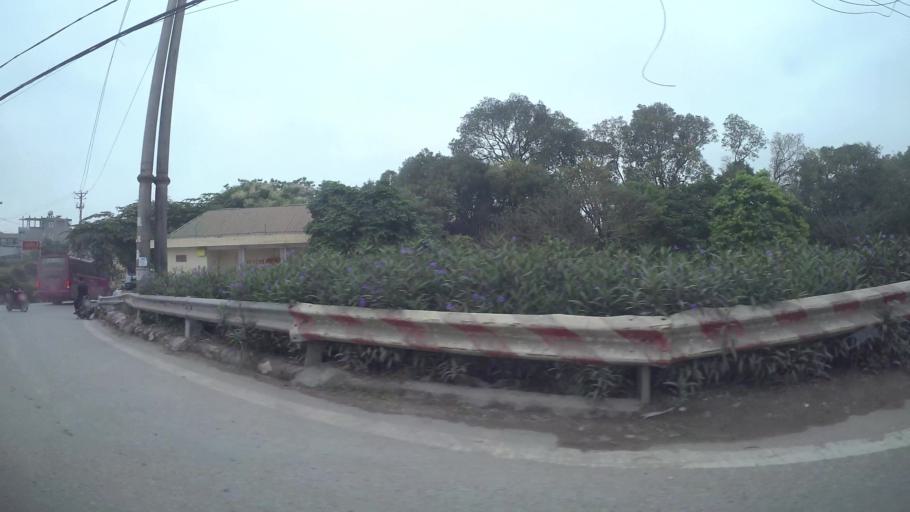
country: VN
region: Ha Noi
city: Hai BaTrung
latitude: 20.9934
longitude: 105.8924
